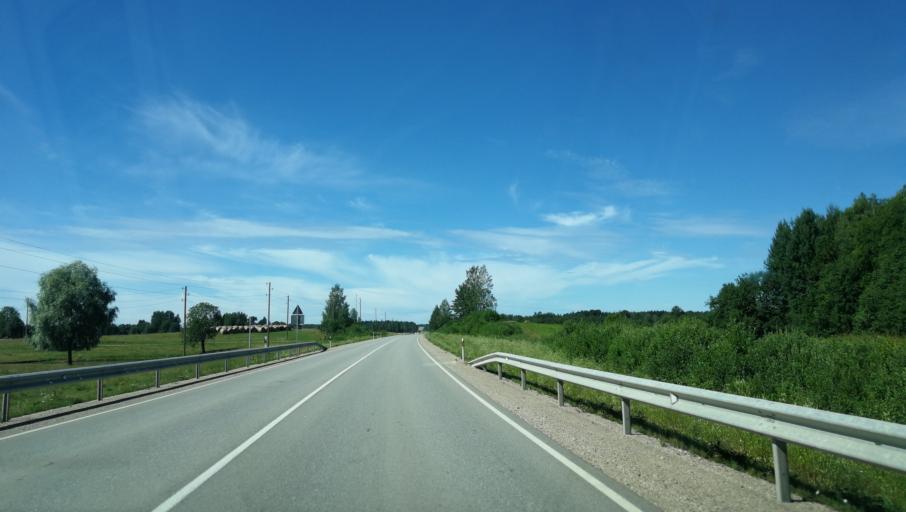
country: LV
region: Gulbenes Rajons
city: Gulbene
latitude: 57.0834
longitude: 26.6089
